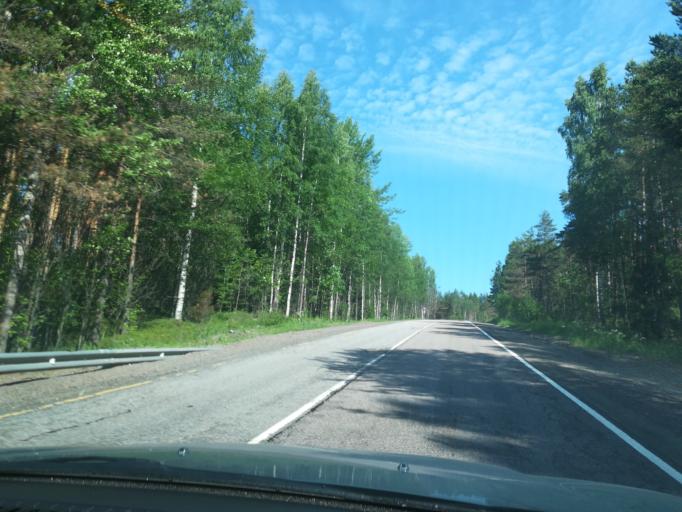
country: RU
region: Leningrad
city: Lesogorskiy
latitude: 60.9188
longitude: 28.8882
